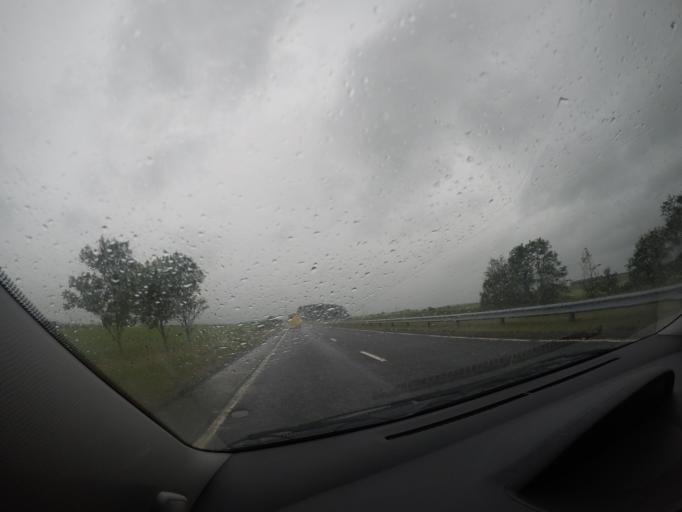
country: GB
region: Scotland
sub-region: Angus
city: Forfar
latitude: 56.6619
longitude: -2.9132
